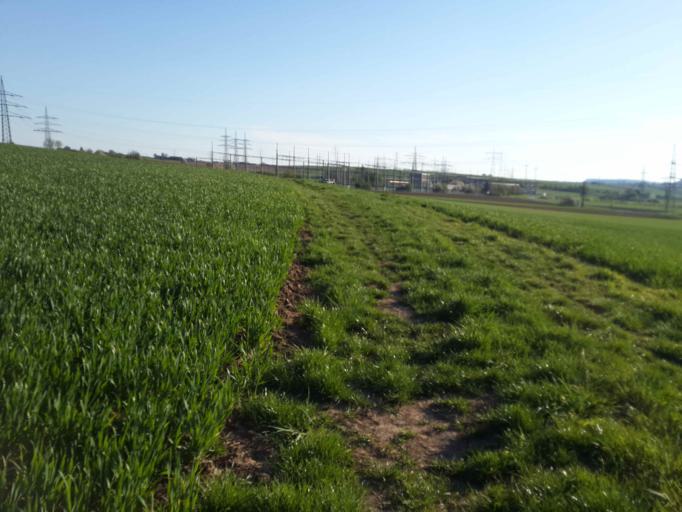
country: DE
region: Baden-Wuerttemberg
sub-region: Regierungsbezirk Stuttgart
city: Leingarten
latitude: 49.1479
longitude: 9.1558
